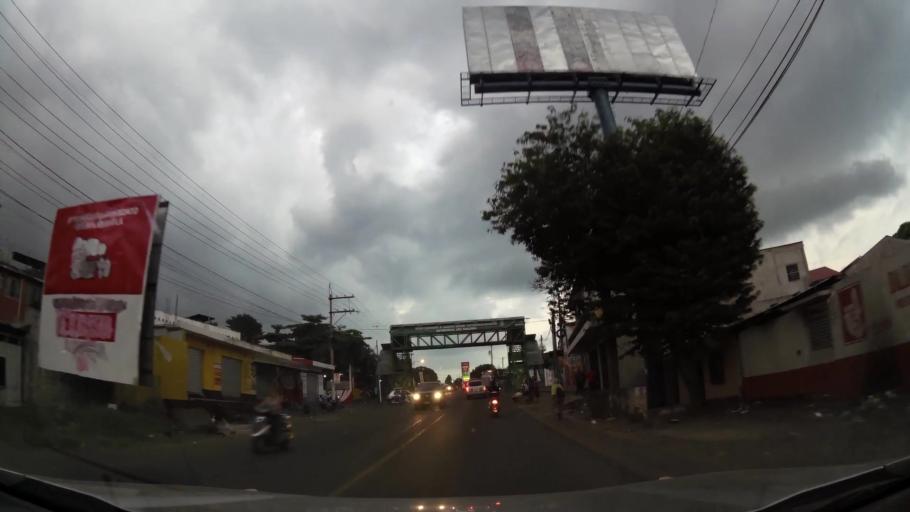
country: GT
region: Escuintla
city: Santa Lucia Cotzumalguapa
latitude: 14.3279
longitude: -91.0246
